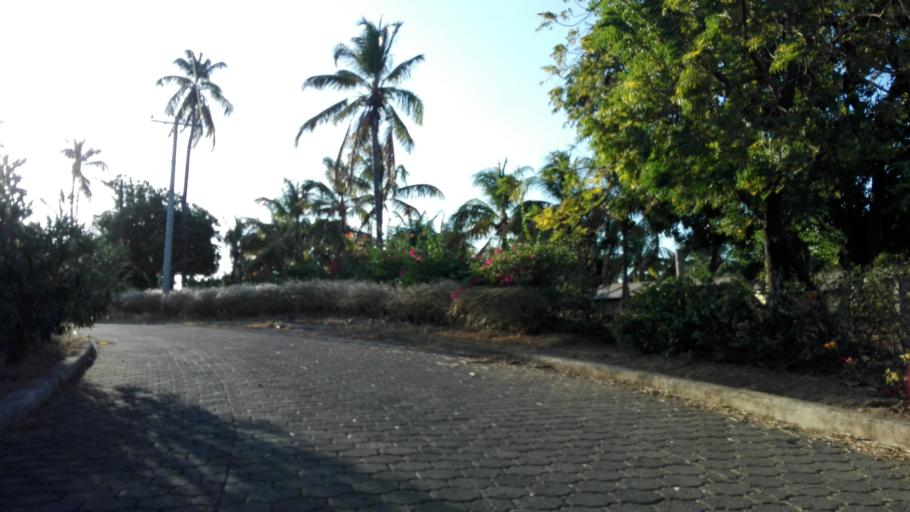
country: NI
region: Managua
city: Managua
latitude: 12.1146
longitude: -86.2432
